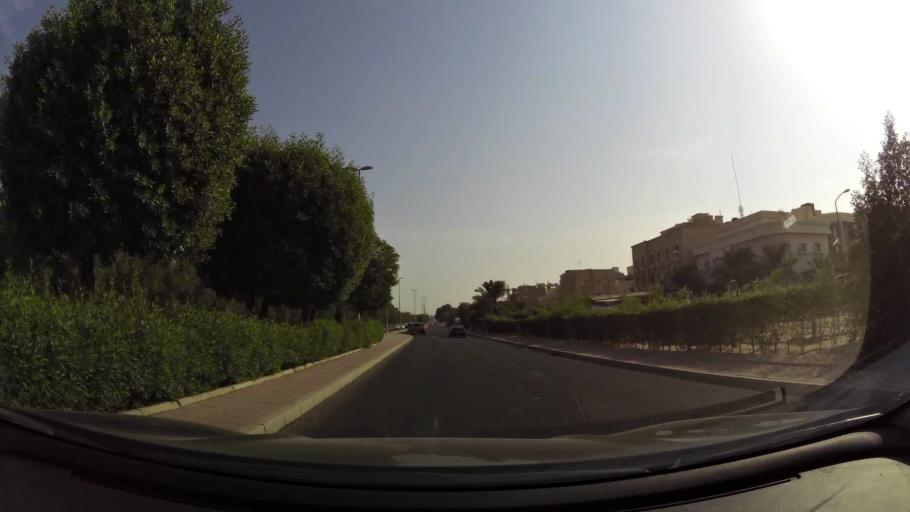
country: KW
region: Mubarak al Kabir
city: Mubarak al Kabir
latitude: 29.1912
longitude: 48.0983
